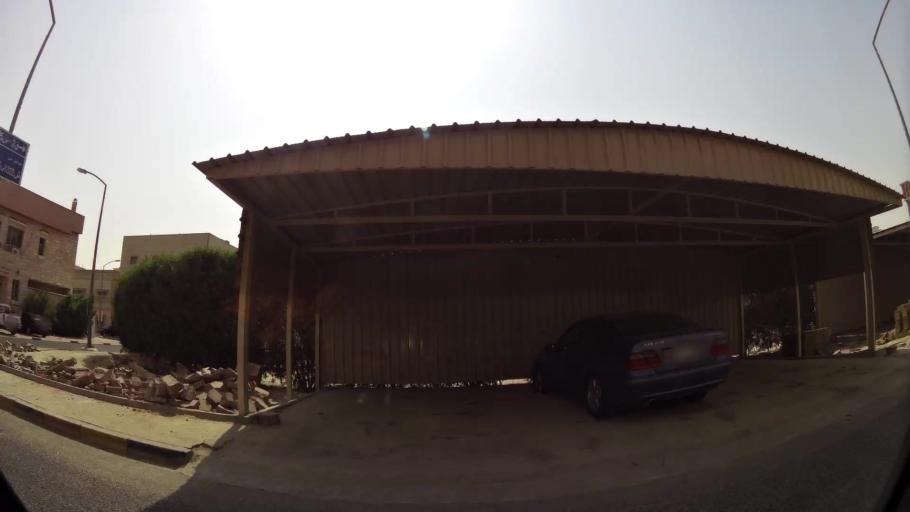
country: KW
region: Muhafazat al Jahra'
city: Al Jahra'
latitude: 29.3028
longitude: 47.7103
